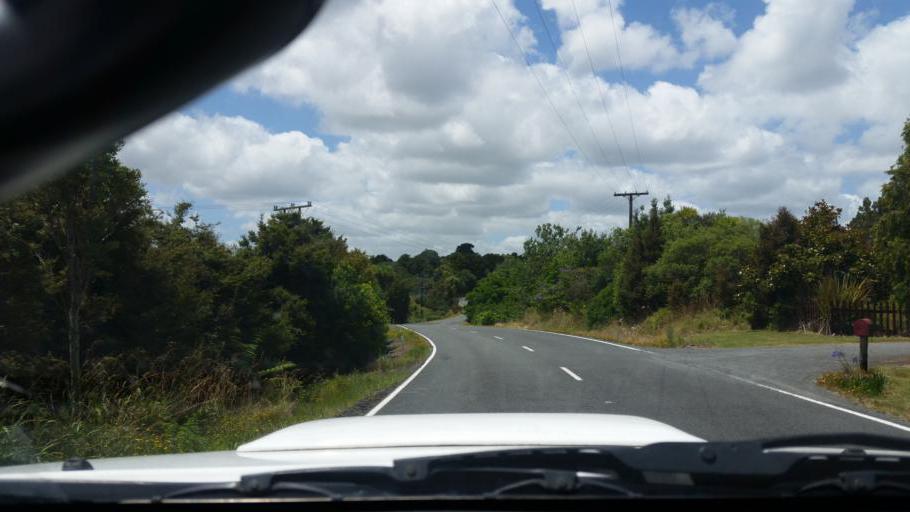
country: NZ
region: Northland
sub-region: Whangarei
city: Ruakaka
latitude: -36.0752
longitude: 174.2593
